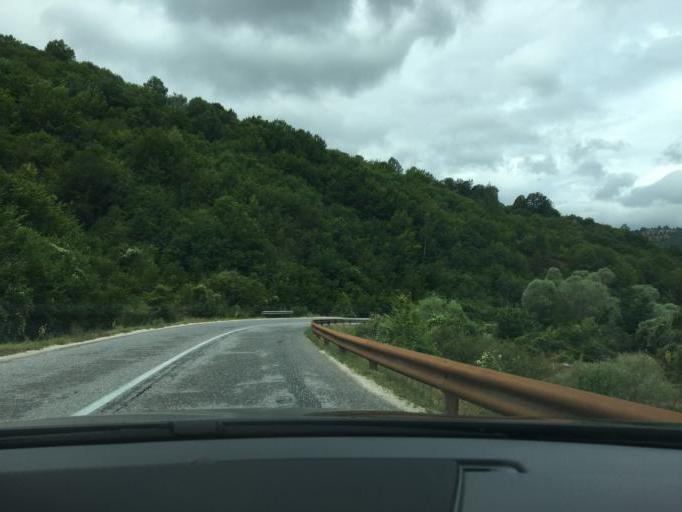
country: MK
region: Kriva Palanka
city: Kriva Palanka
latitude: 42.2293
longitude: 22.3756
